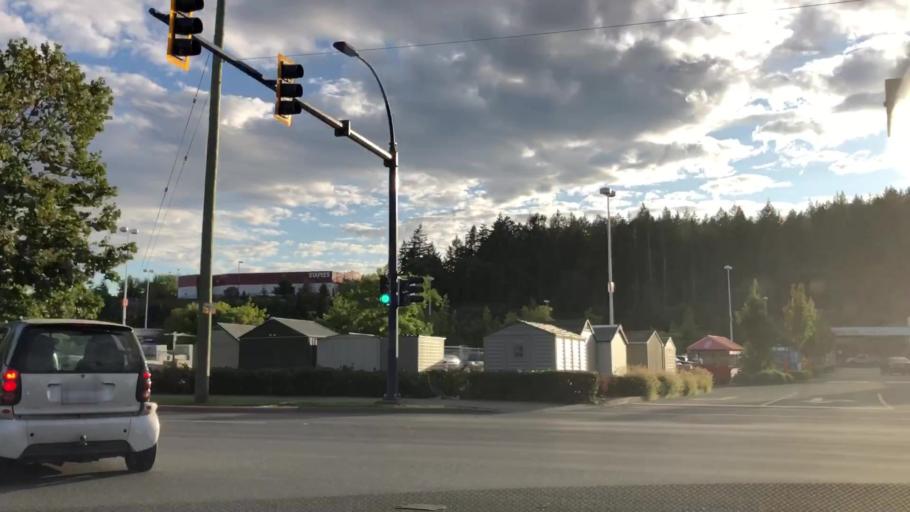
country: CA
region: British Columbia
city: Langford
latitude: 48.4618
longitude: -123.4978
